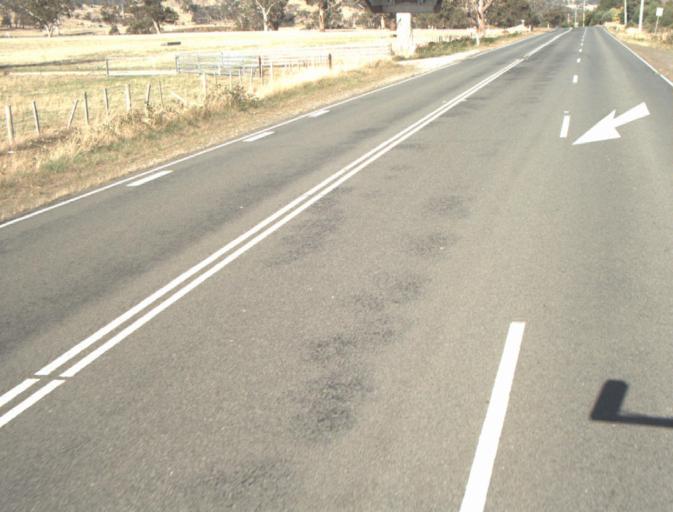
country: AU
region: Tasmania
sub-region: Launceston
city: Mayfield
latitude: -41.3413
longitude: 147.0881
